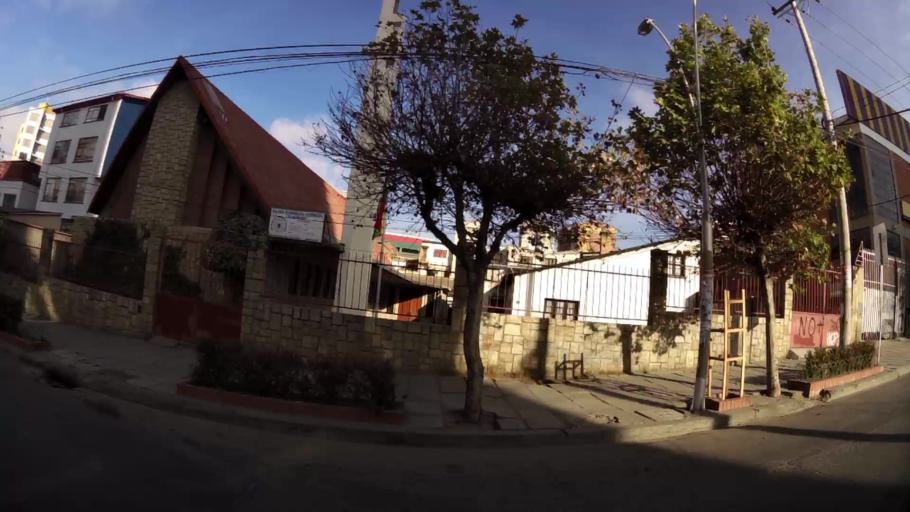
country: BO
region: La Paz
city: La Paz
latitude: -16.4989
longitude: -68.1212
